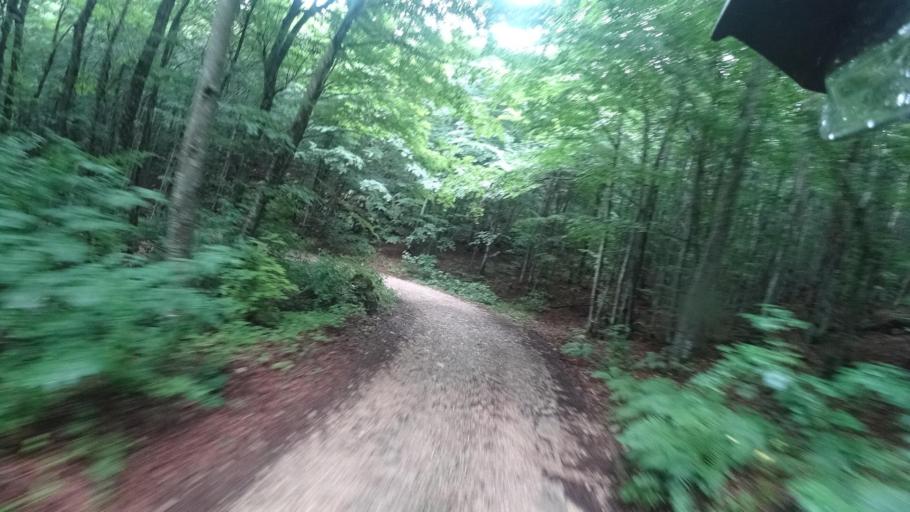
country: HR
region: Licko-Senjska
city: Jezerce
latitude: 44.7478
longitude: 15.6306
